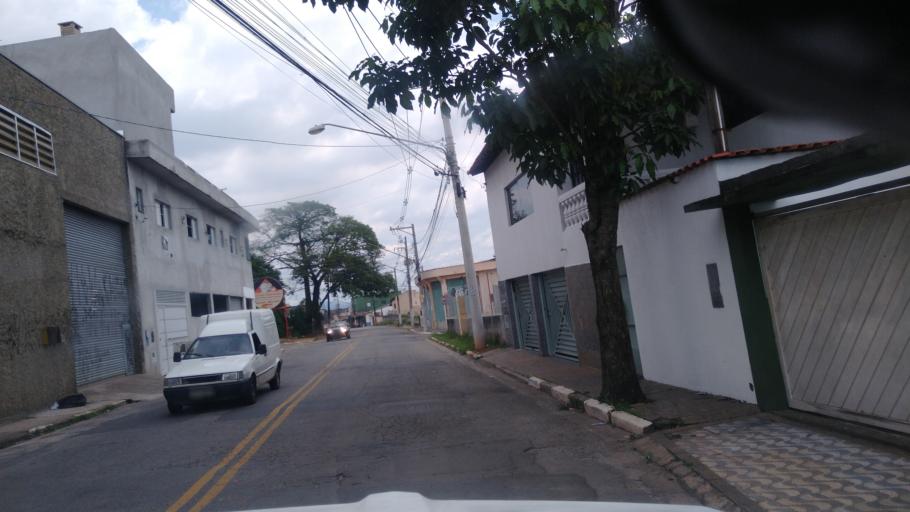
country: BR
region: Sao Paulo
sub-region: Suzano
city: Suzano
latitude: -23.5582
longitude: -46.3218
